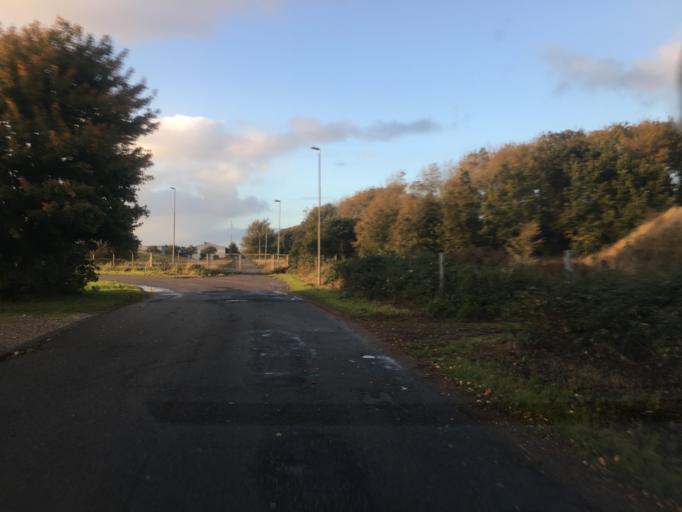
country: DK
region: South Denmark
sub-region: Tonder Kommune
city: Tonder
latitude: 54.9226
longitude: 8.8533
